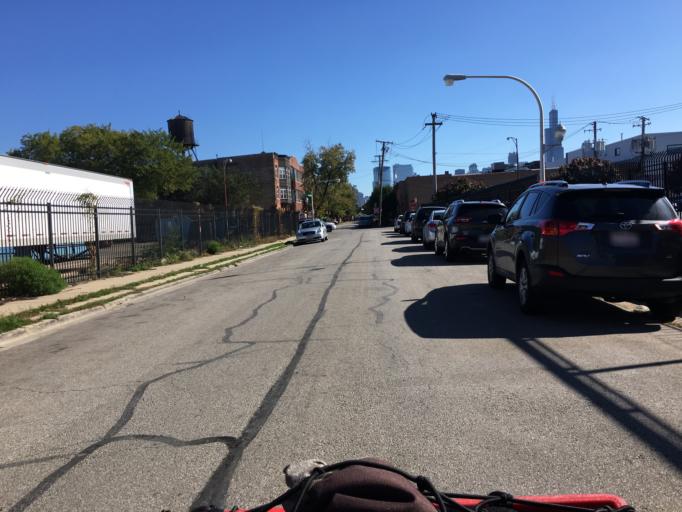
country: US
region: Illinois
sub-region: Cook County
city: Chicago
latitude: 41.8860
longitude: -87.6703
